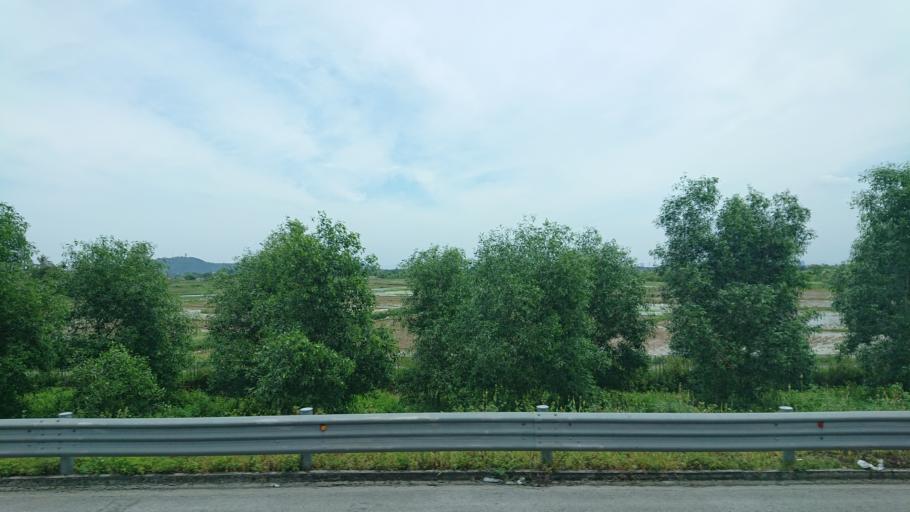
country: VN
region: Hai Phong
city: Nui Doi
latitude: 20.7673
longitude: 106.6399
